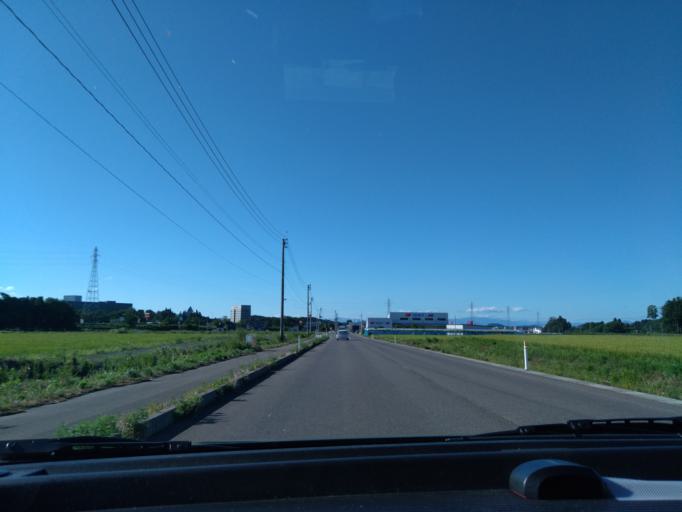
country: JP
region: Akita
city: Yokotemachi
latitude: 39.2863
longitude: 140.5553
